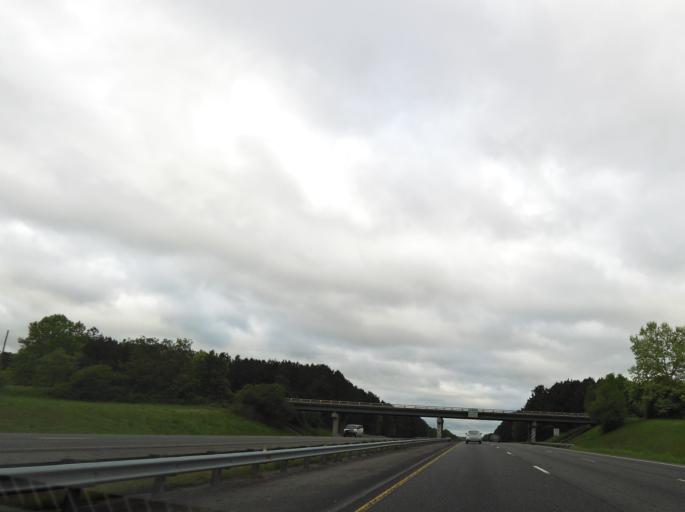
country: US
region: Georgia
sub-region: Butts County
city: Indian Springs
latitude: 33.1678
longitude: -84.0411
